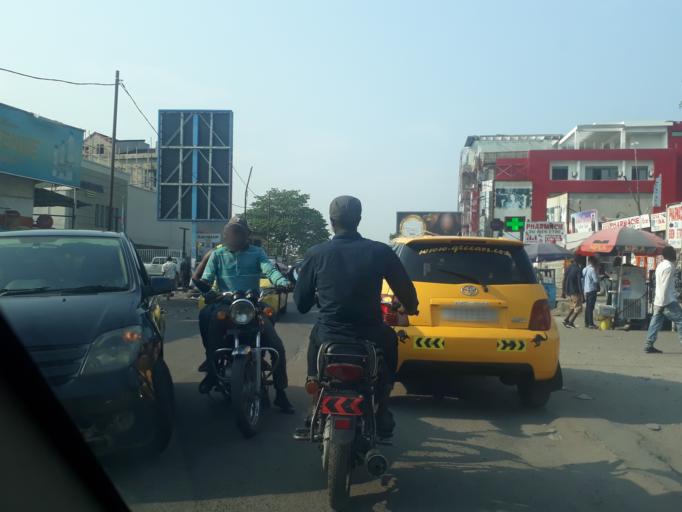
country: CD
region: Kinshasa
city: Kinshasa
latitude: -4.3213
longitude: 15.3294
